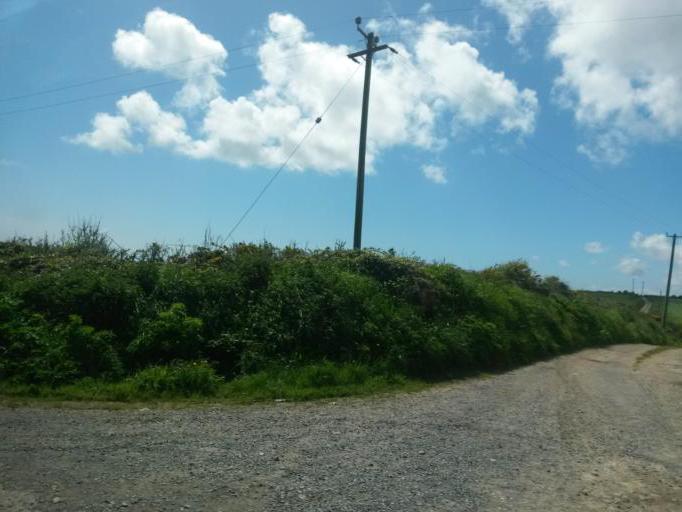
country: IE
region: Munster
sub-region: Waterford
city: Dunmore East
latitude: 52.1820
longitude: -6.8948
